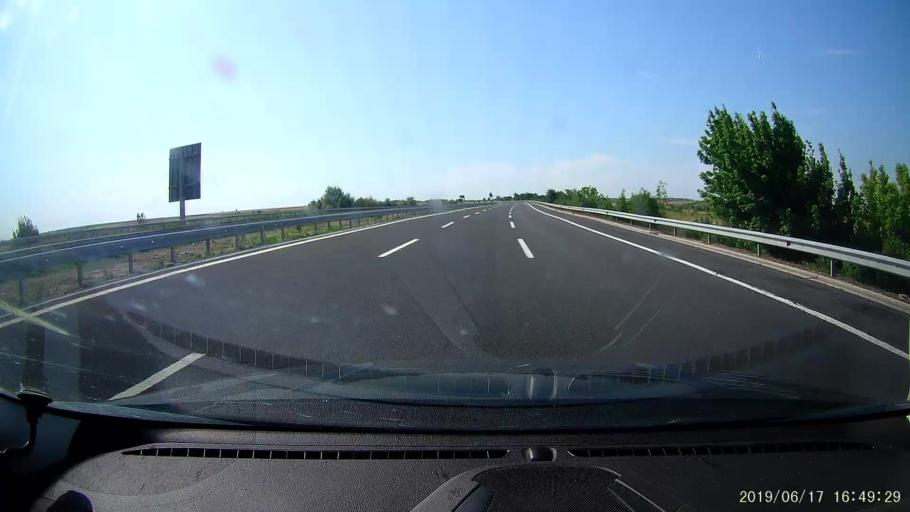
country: TR
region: Kirklareli
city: Babaeski
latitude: 41.5092
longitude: 27.1117
